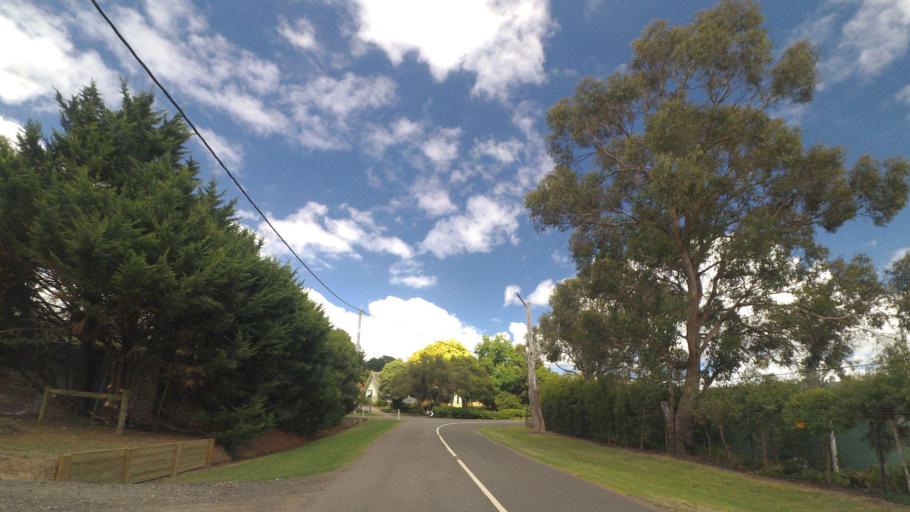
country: AU
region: Victoria
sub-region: Knox
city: The Basin
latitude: -37.8470
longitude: 145.3161
